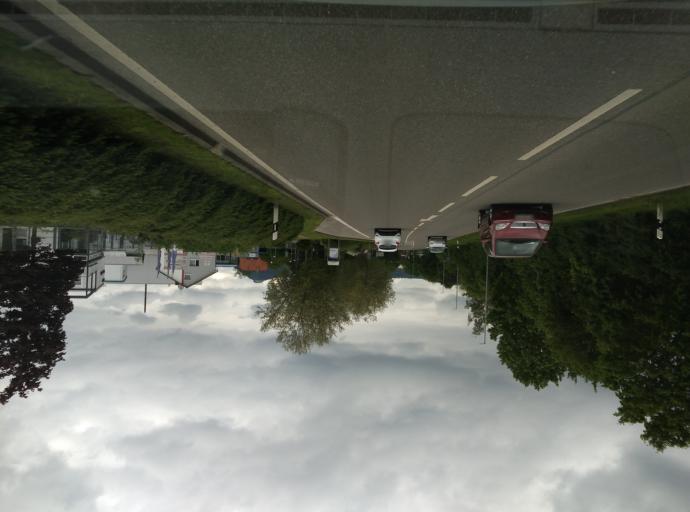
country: DE
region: Baden-Wuerttemberg
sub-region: Regierungsbezirk Stuttgart
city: Frickenhausen
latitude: 48.6001
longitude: 9.3512
